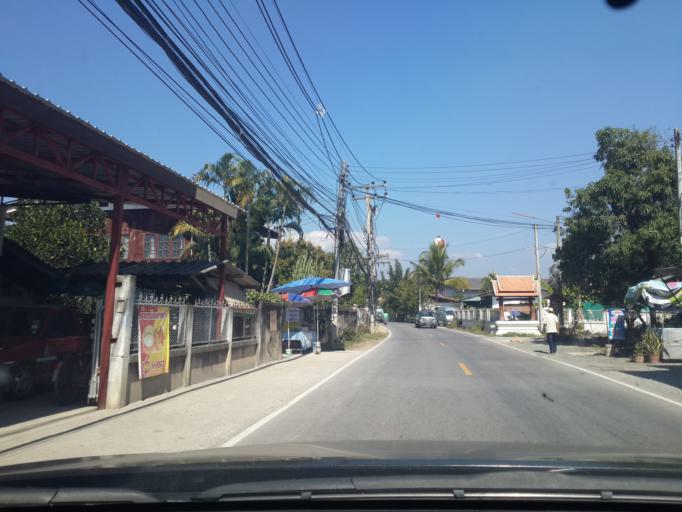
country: TH
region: Chiang Mai
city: San Sai
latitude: 18.8540
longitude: 99.0880
